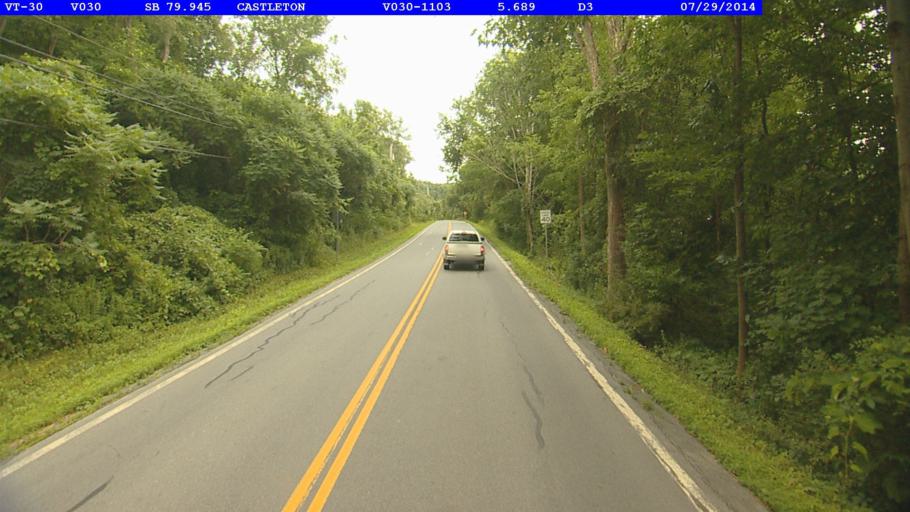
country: US
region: Vermont
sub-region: Rutland County
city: Castleton
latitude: 43.6666
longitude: -73.1916
